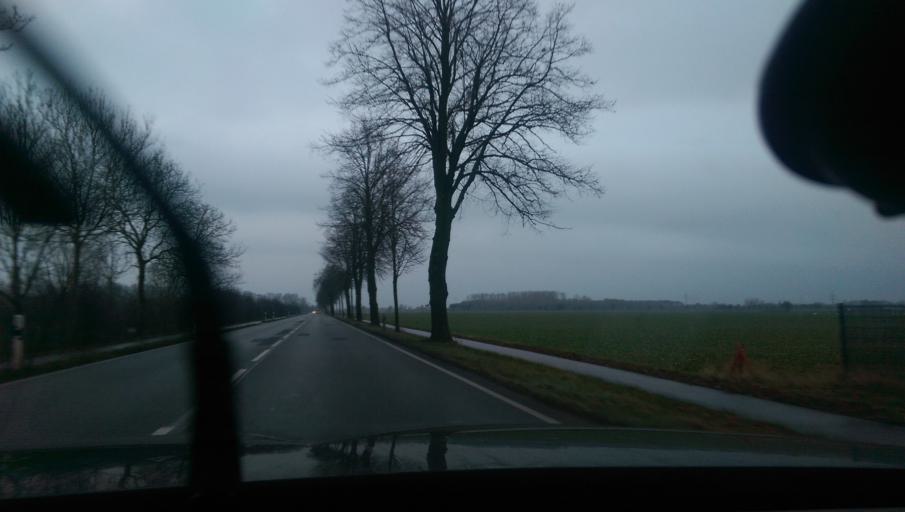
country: DE
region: Lower Saxony
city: Verden
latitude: 52.9116
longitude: 9.2171
